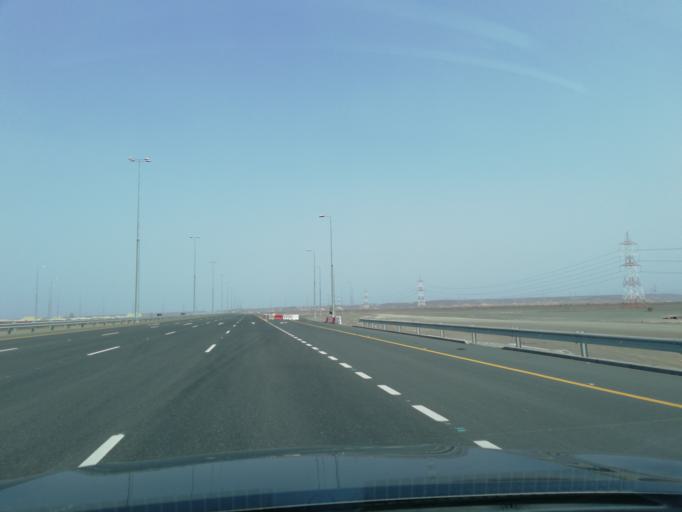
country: OM
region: Al Batinah
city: Al Sohar
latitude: 24.3185
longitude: 56.5762
